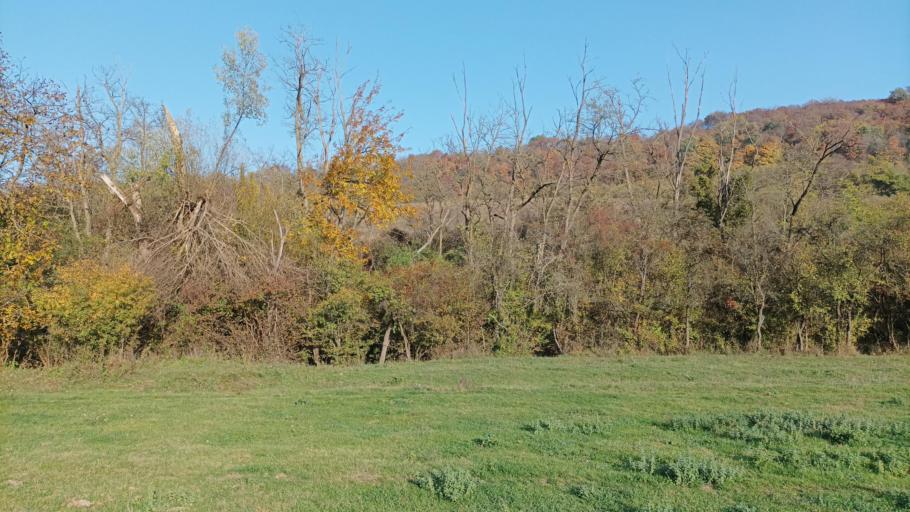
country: HU
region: Tolna
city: Szentgalpuszta
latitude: 46.3320
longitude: 18.6070
